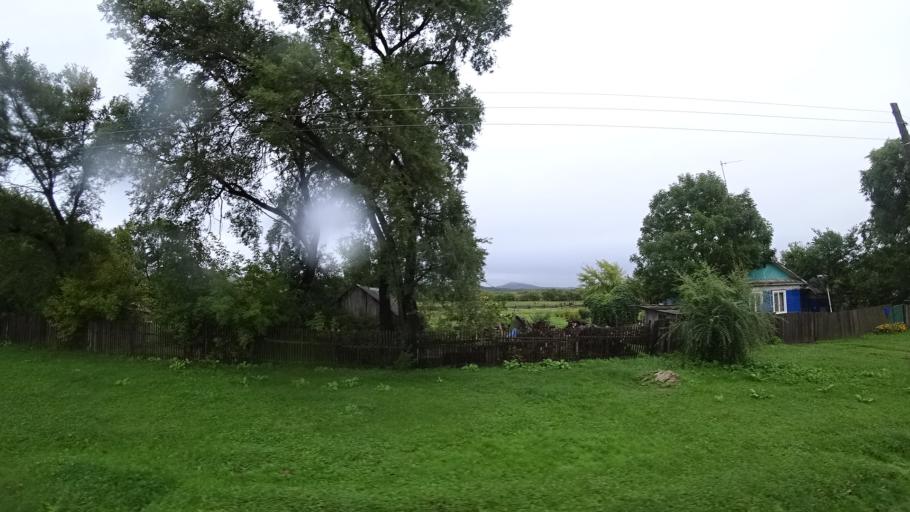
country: RU
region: Primorskiy
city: Monastyrishche
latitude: 44.2533
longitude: 132.4265
